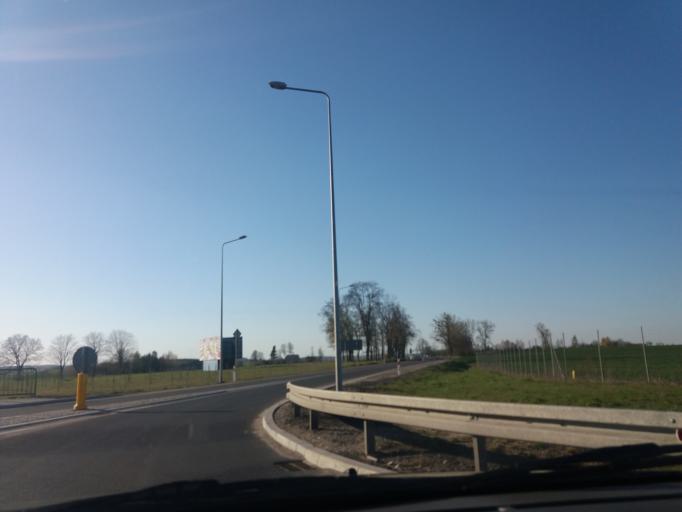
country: PL
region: Warmian-Masurian Voivodeship
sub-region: Powiat nidzicki
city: Nidzica
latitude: 53.3342
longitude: 20.4390
